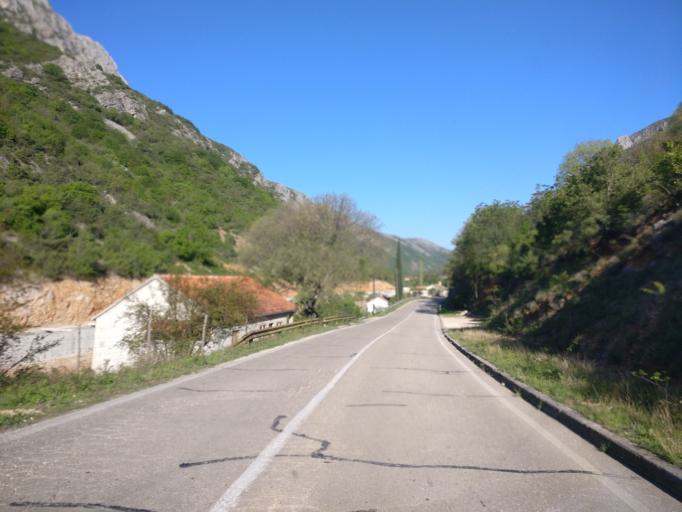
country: BA
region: Federation of Bosnia and Herzegovina
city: Stolac
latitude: 43.0739
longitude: 18.0309
